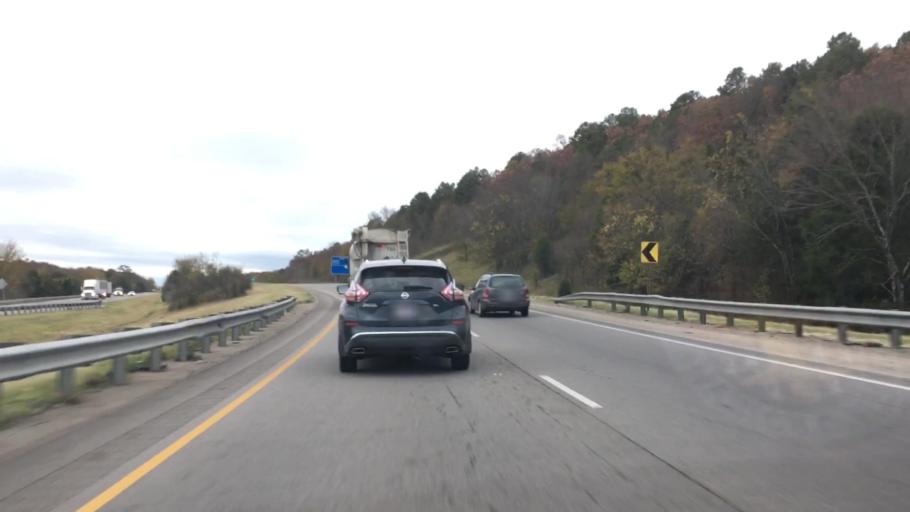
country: US
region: Arkansas
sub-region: Johnson County
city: Coal Hill
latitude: 35.5032
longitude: -93.7307
